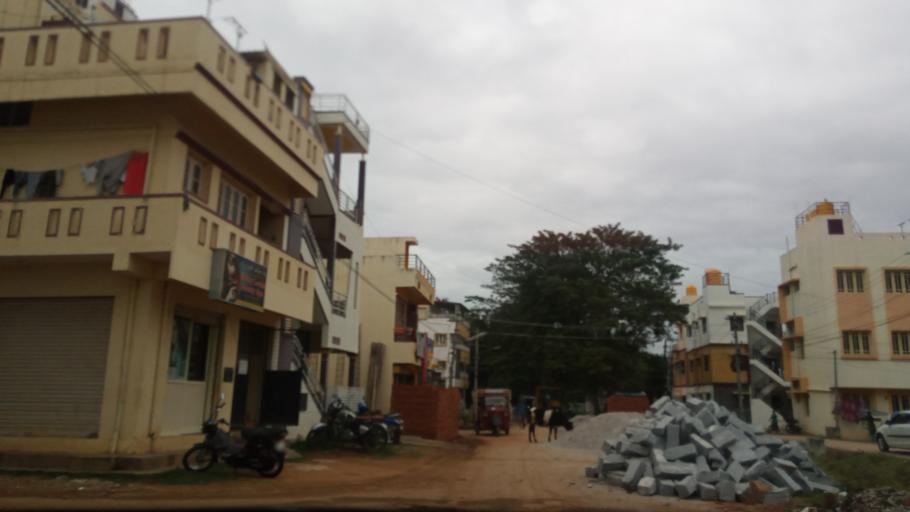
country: IN
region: Karnataka
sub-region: Mysore
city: Mysore
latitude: 12.2954
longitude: 76.6059
